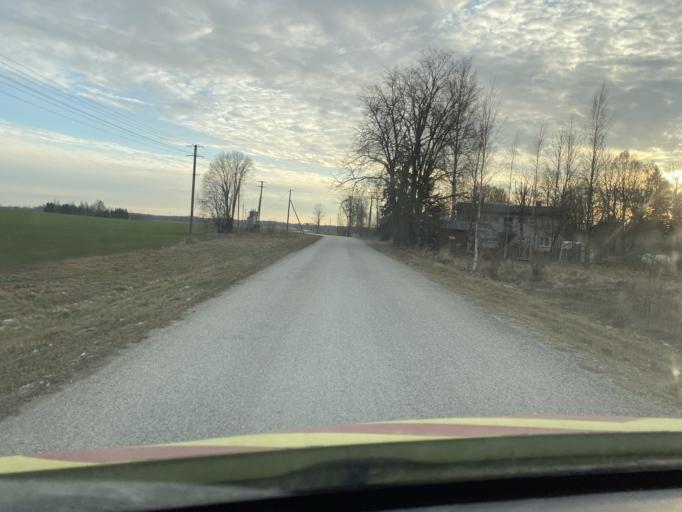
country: EE
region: Jogevamaa
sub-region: Poltsamaa linn
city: Poltsamaa
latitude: 58.5841
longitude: 26.1049
